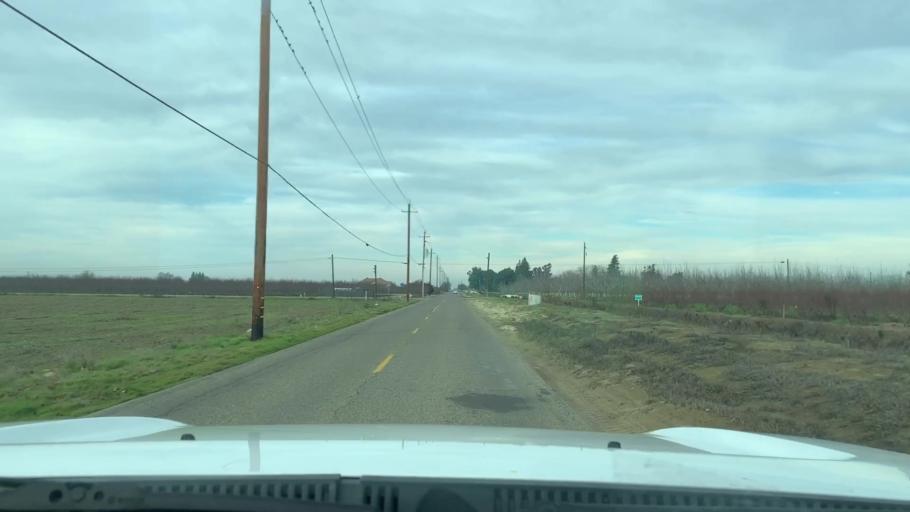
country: US
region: California
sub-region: Fresno County
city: Selma
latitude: 36.5748
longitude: -119.5749
